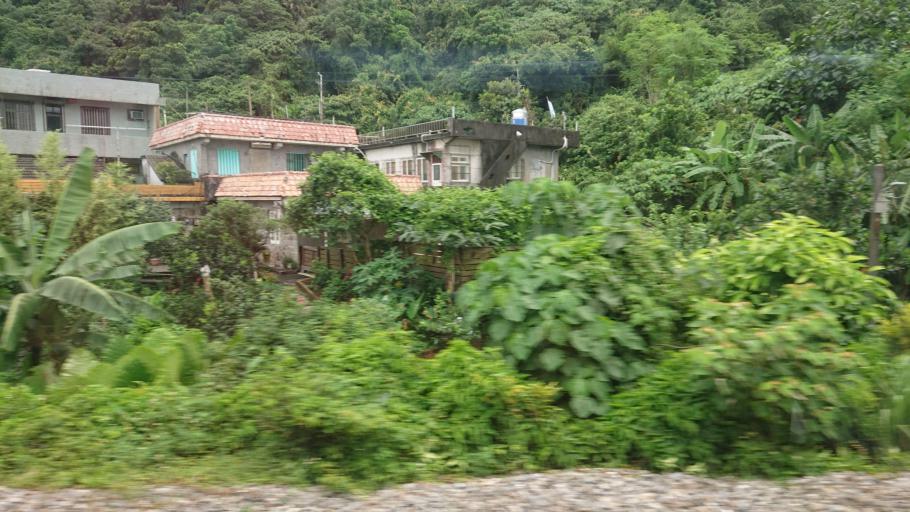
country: TW
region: Taiwan
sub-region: Keelung
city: Keelung
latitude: 24.9802
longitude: 121.9499
